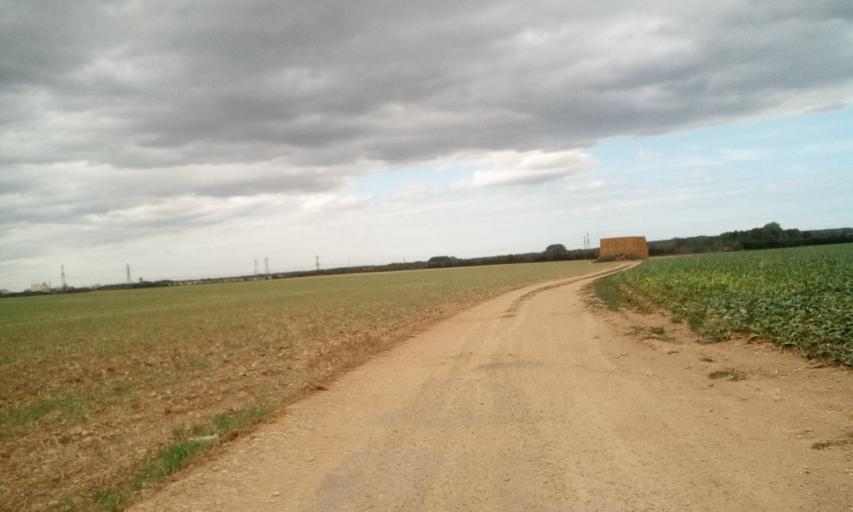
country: FR
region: Lower Normandy
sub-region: Departement du Calvados
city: Bellengreville
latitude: 49.1201
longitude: -0.2243
